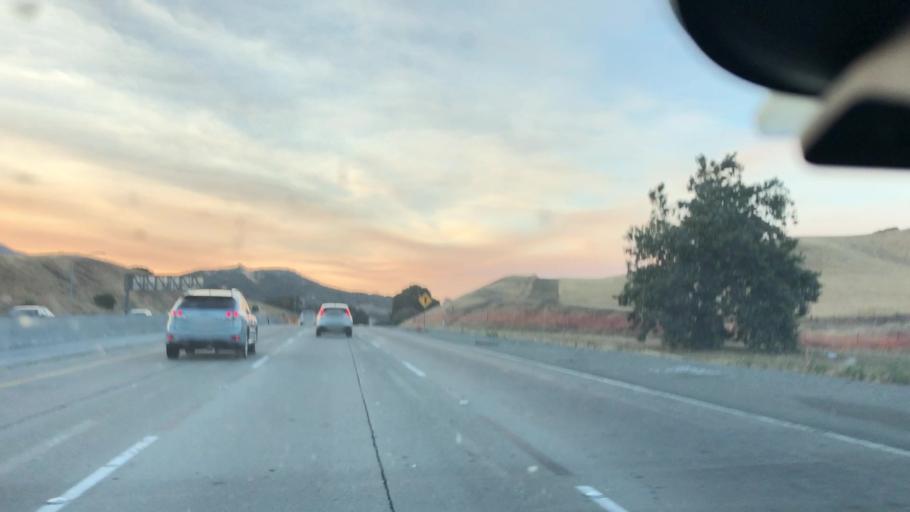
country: US
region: California
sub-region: Alameda County
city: Pleasanton
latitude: 37.5940
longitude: -121.8713
